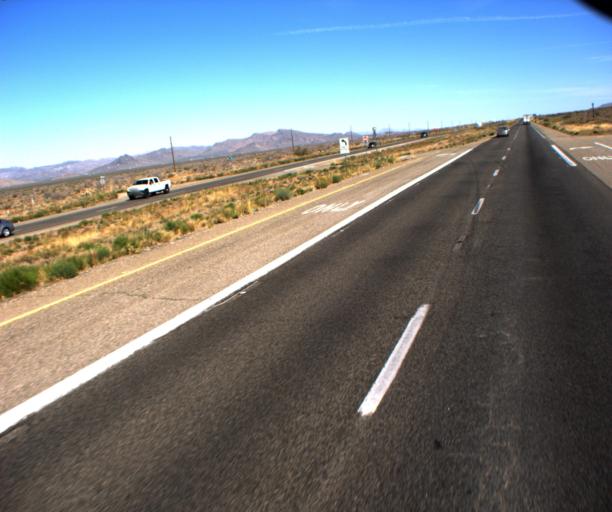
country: US
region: Arizona
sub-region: Mohave County
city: Golden Valley
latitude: 35.2806
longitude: -114.1749
